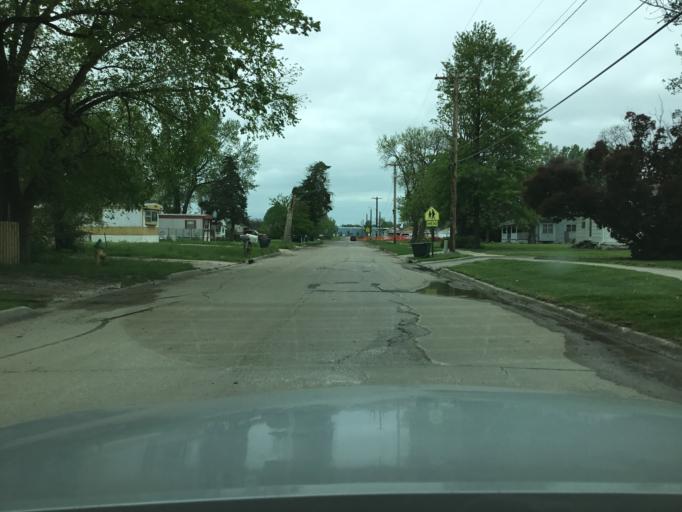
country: US
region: Kansas
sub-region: Franklin County
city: Ottawa
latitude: 38.6333
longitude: -95.2586
